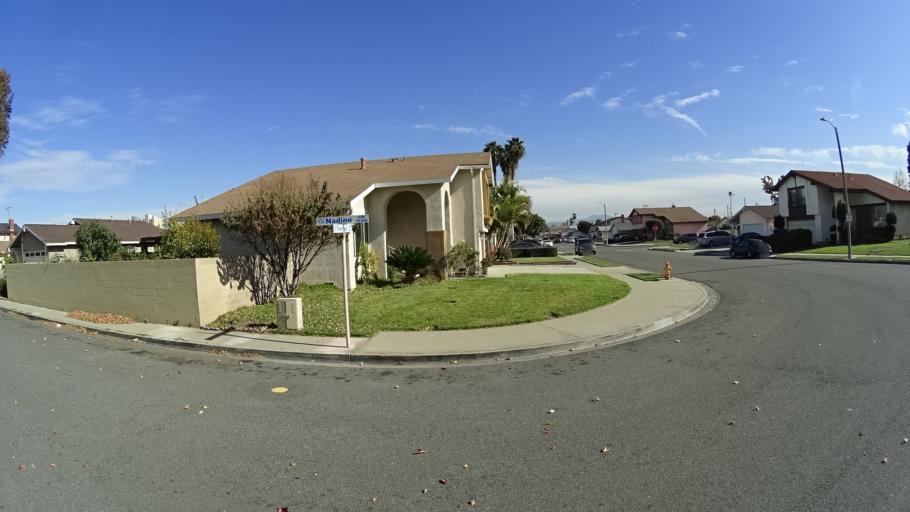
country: US
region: California
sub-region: Orange County
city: Garden Grove
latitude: 33.7839
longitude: -117.9209
